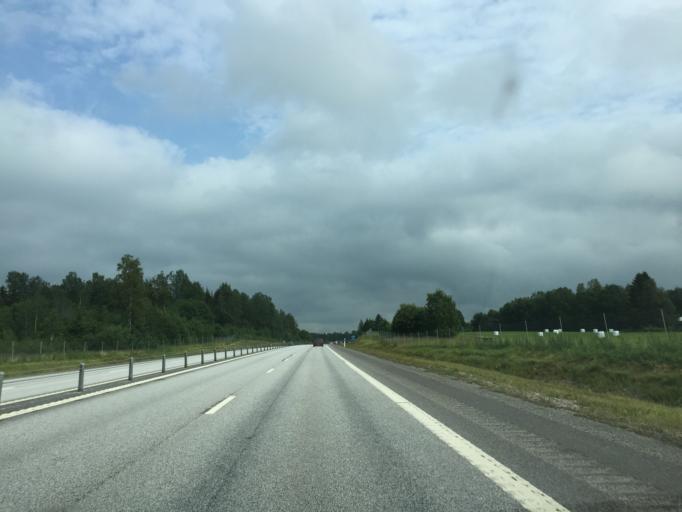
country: SE
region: OErebro
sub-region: Orebro Kommun
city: Vintrosa
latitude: 59.2531
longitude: 14.9076
